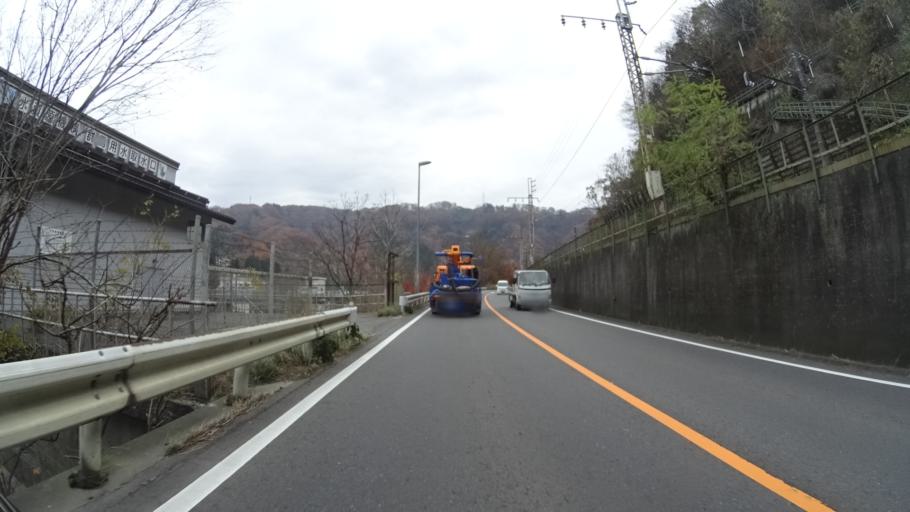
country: JP
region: Gunma
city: Numata
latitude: 36.5892
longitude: 139.0535
